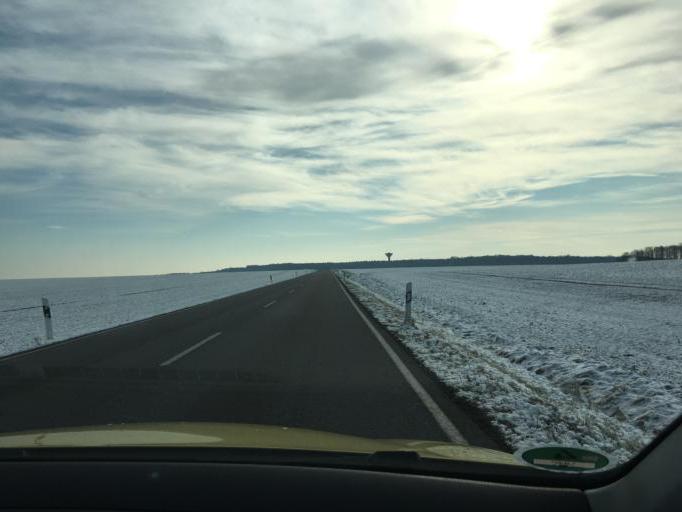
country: DE
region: Saxony
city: Geithain
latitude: 51.0956
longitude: 12.7015
